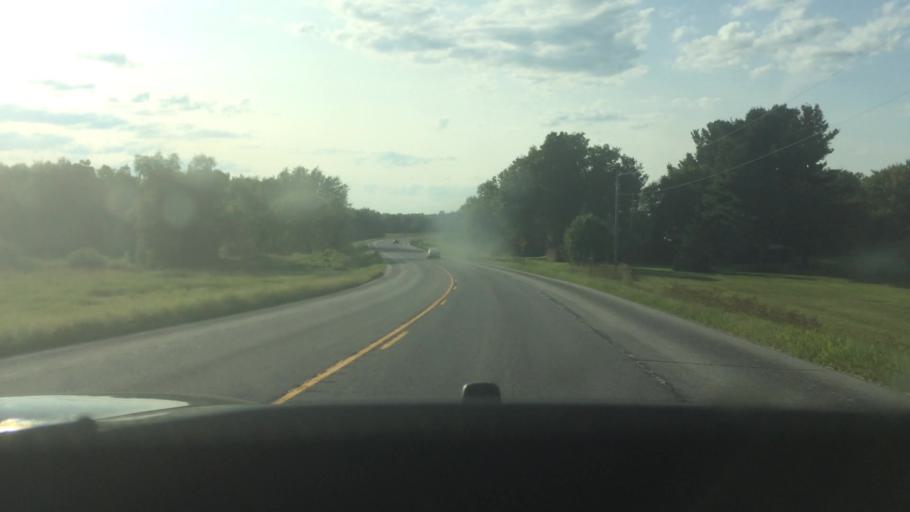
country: US
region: New York
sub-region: St. Lawrence County
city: Canton
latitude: 44.6066
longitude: -75.2075
